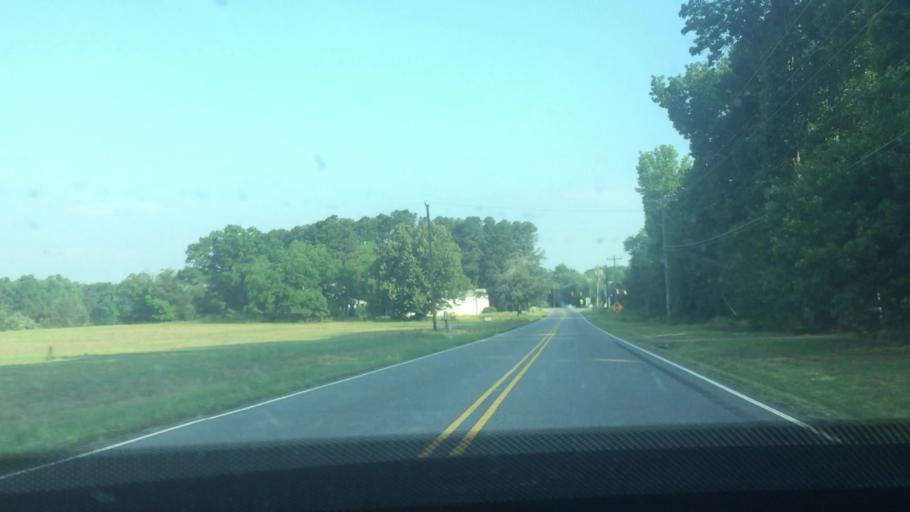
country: US
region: North Carolina
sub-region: Iredell County
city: Mooresville
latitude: 35.5960
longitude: -80.7620
